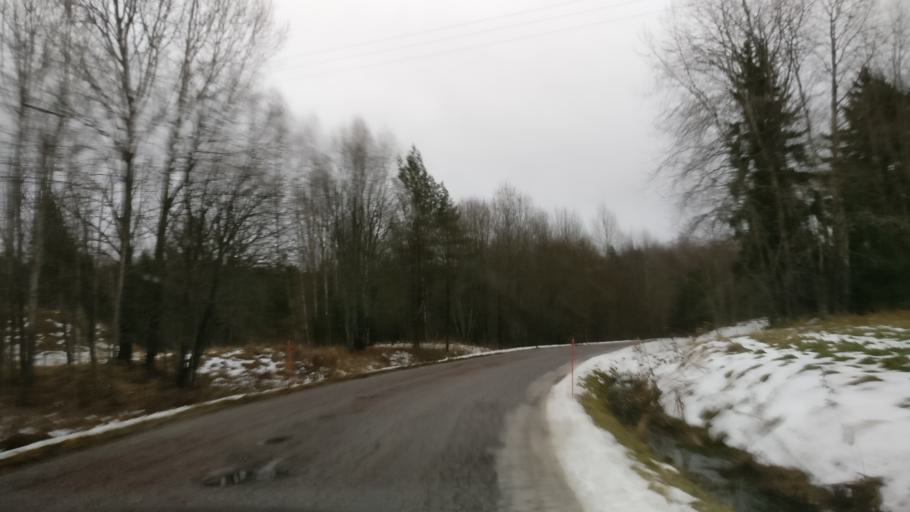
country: FI
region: Uusimaa
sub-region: Raaseporin
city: Karis
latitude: 60.0719
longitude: 23.8025
